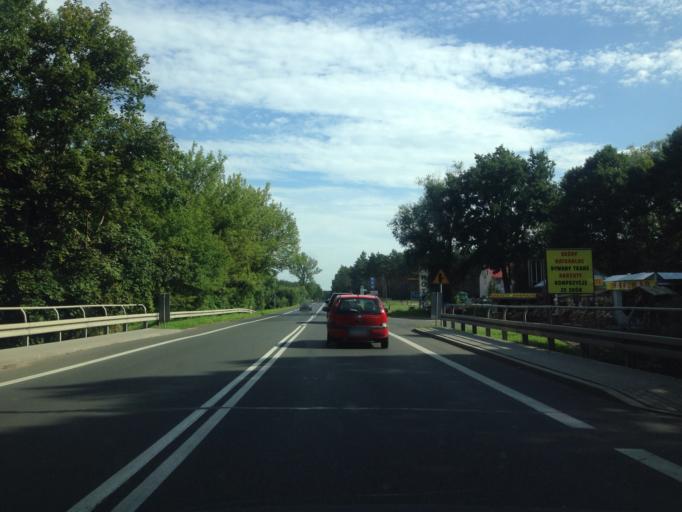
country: PL
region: Kujawsko-Pomorskie
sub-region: Powiat aleksandrowski
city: Aleksandrow Kujawski
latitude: 52.8972
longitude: 18.7277
